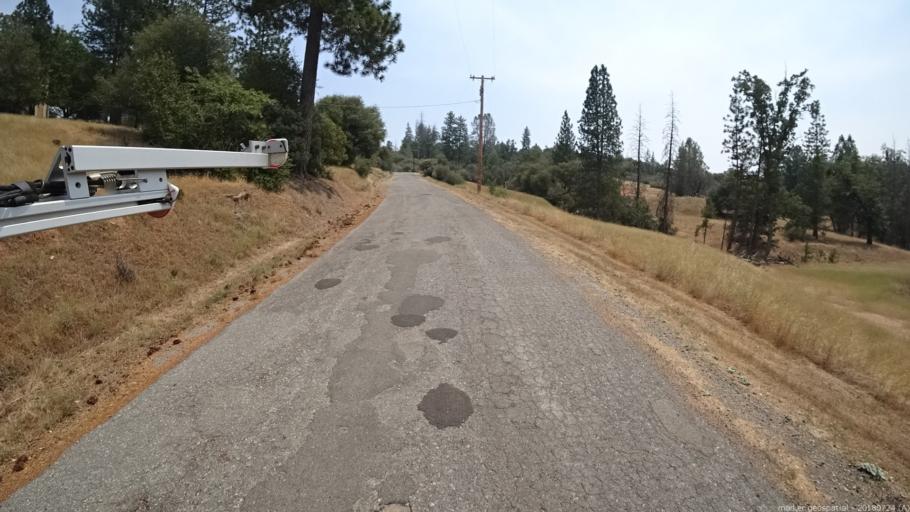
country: US
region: California
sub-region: Madera County
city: Oakhurst
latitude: 37.2474
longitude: -119.5587
